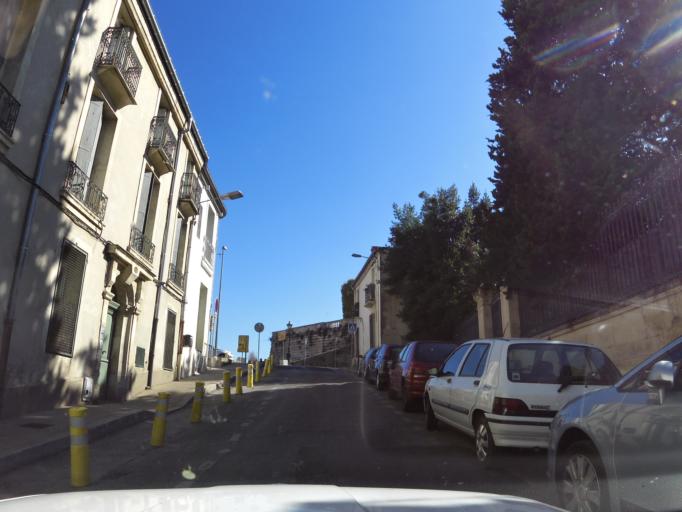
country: FR
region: Languedoc-Roussillon
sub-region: Departement de l'Herault
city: Montpellier
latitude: 43.6124
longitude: 3.8718
